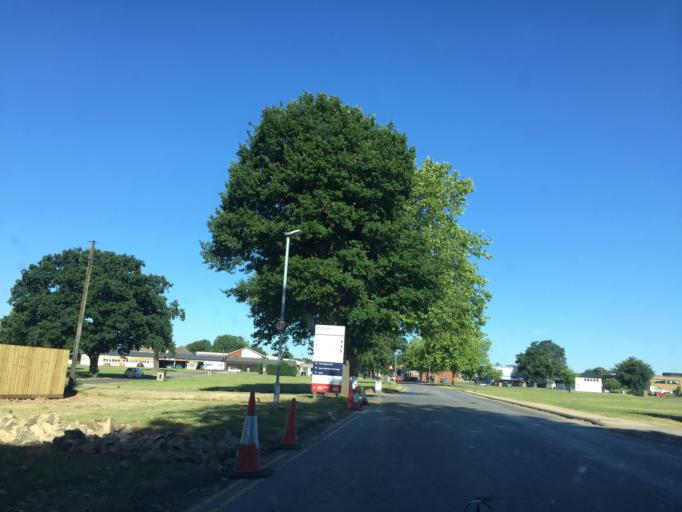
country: GB
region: England
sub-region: Warwickshire
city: Royal Leamington Spa
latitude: 52.3391
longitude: -1.5202
